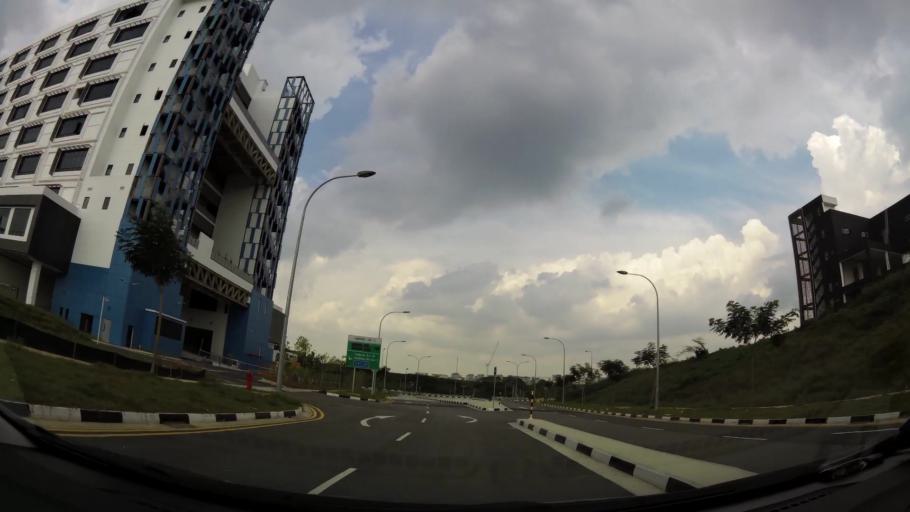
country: SG
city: Singapore
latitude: 1.3650
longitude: 103.9325
